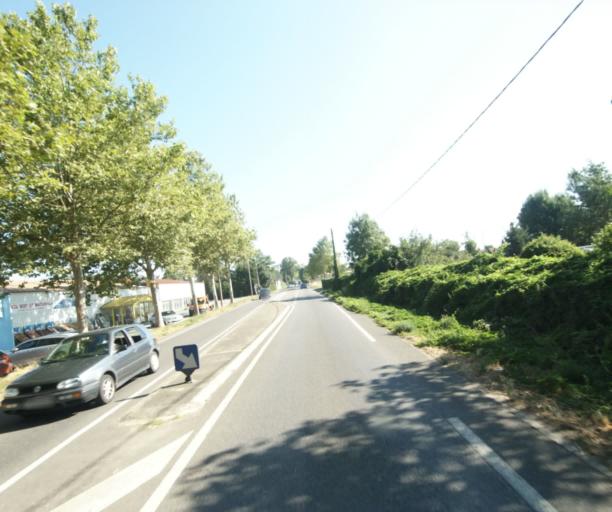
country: FR
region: Midi-Pyrenees
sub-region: Departement de la Haute-Garonne
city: Revel
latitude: 43.4691
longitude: 2.0114
